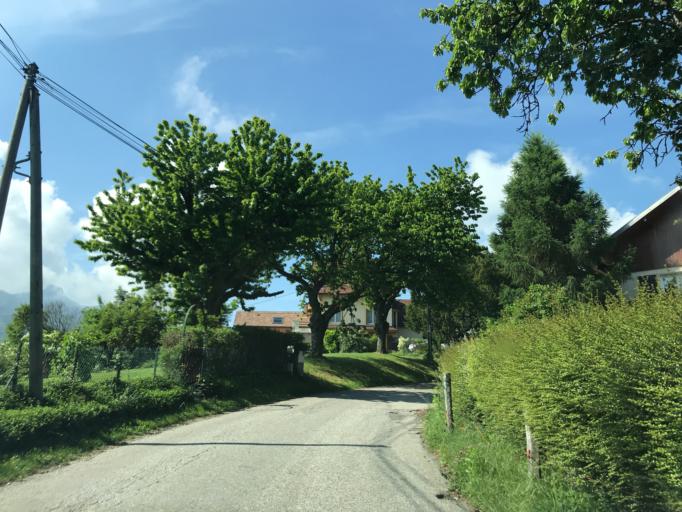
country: FR
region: Rhone-Alpes
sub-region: Departement de la Savoie
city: Vimines
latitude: 45.5494
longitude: 5.8703
